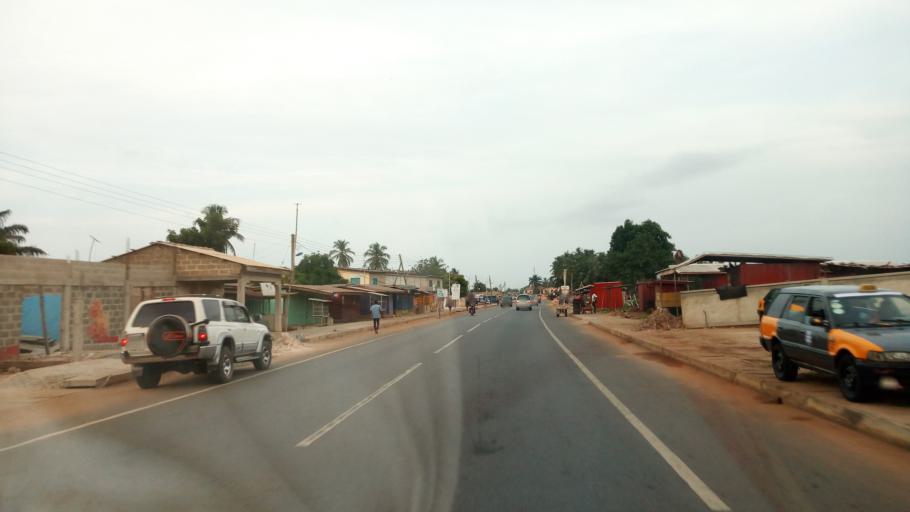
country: TG
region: Maritime
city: Lome
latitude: 6.1055
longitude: 1.1525
